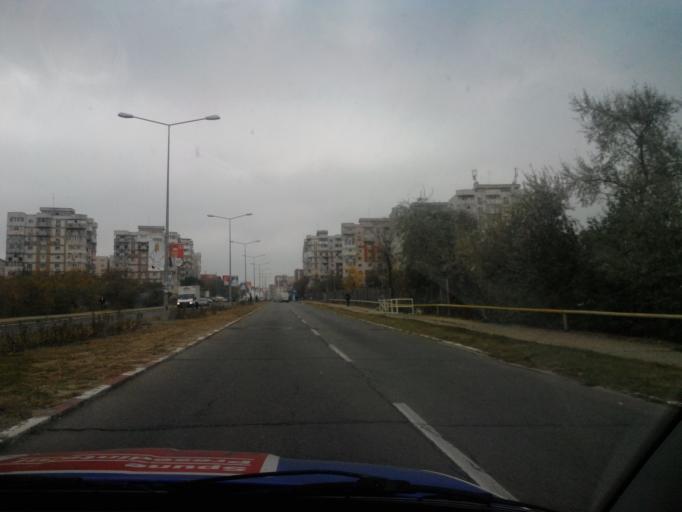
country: RO
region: Galati
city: Galati
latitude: 45.4062
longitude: 28.0152
